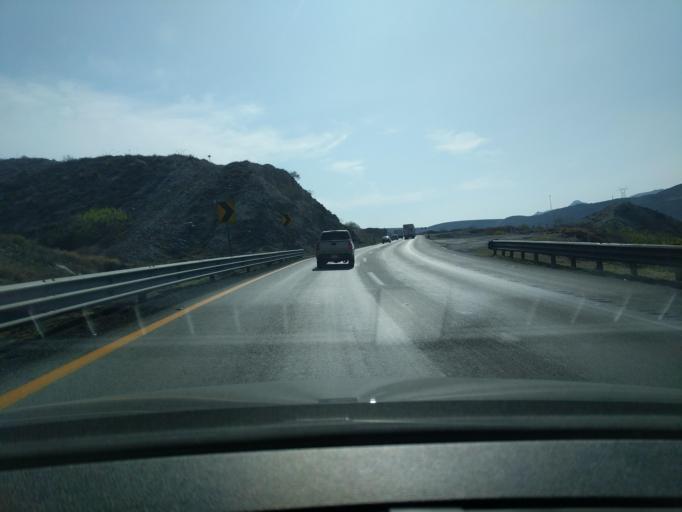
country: MX
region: Nuevo Leon
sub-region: Garcia
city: Las Torres de Guadalupe
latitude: 25.6518
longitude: -100.7289
